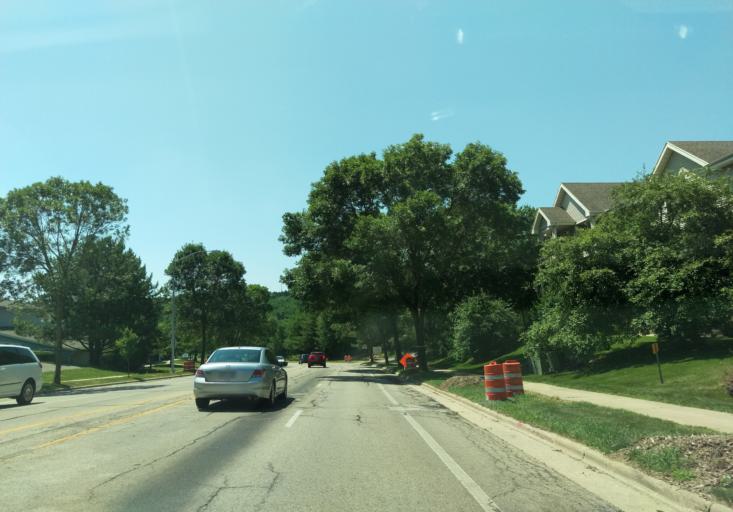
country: US
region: Wisconsin
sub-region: Dane County
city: Middleton
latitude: 43.0415
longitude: -89.5049
